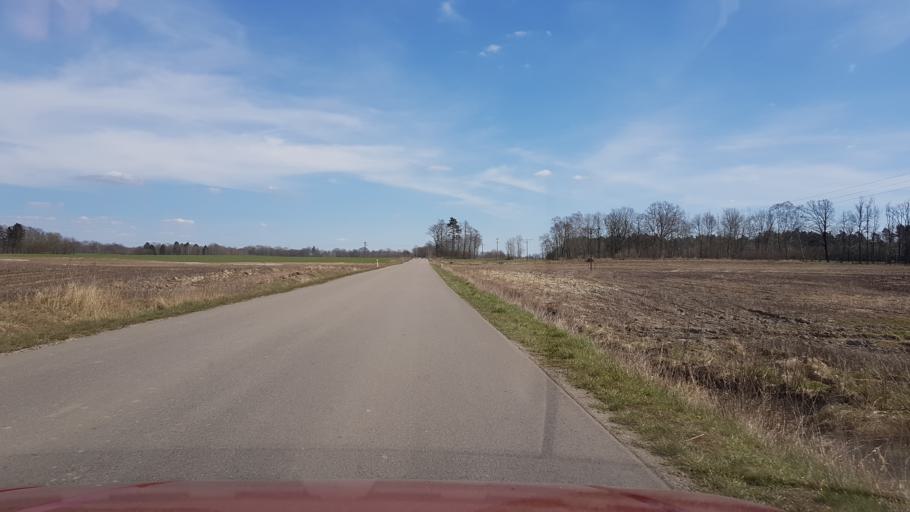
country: PL
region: West Pomeranian Voivodeship
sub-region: Powiat koszalinski
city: Mielno
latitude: 54.1580
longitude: 16.0525
